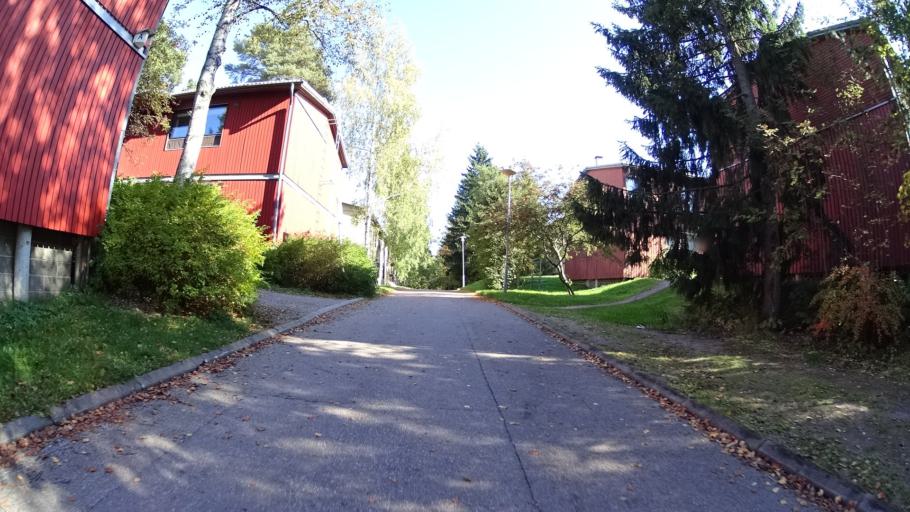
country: FI
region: Uusimaa
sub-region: Helsinki
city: Kilo
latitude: 60.2218
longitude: 24.7784
